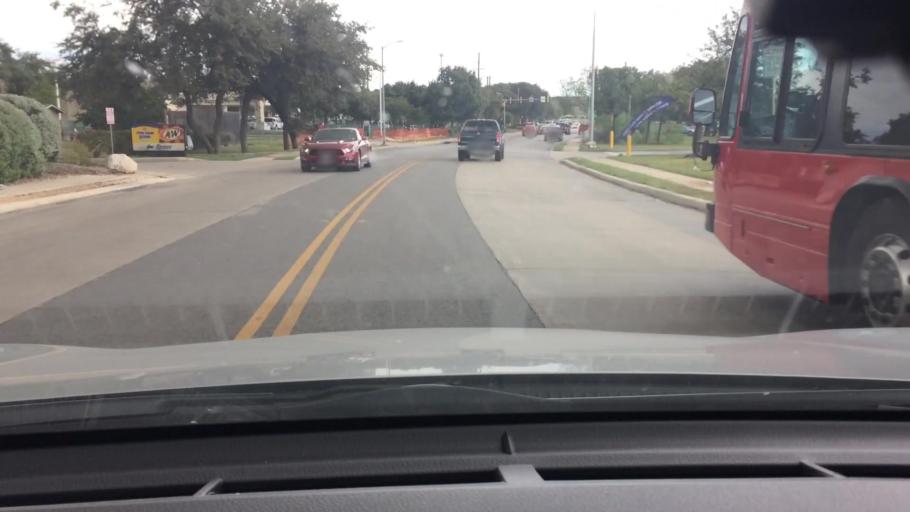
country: US
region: Texas
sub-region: Bexar County
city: Shavano Park
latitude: 29.5646
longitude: -98.5937
